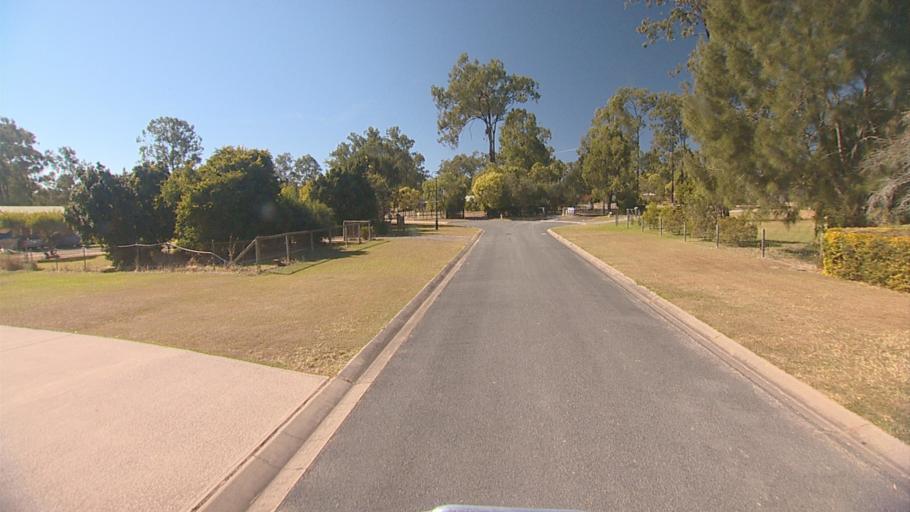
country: AU
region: Queensland
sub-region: Logan
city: North Maclean
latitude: -27.8190
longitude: 152.9552
